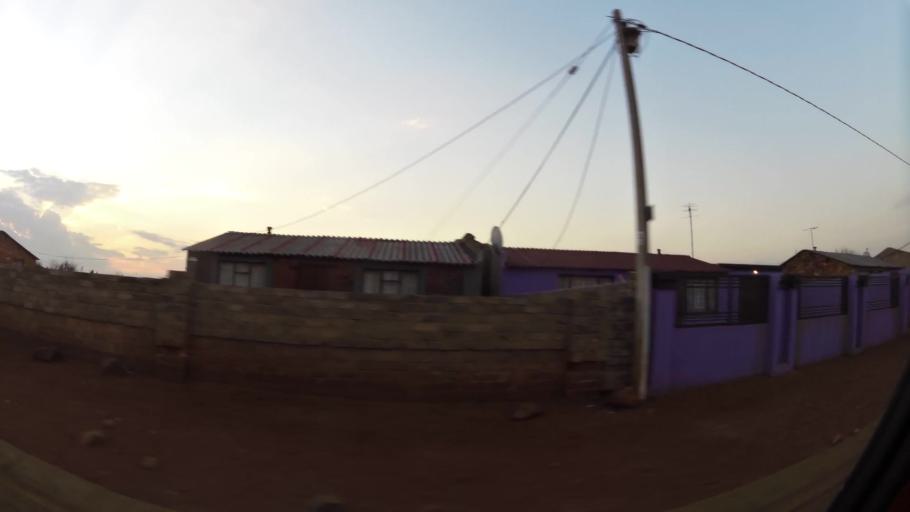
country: ZA
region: Gauteng
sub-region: City of Johannesburg Metropolitan Municipality
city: Orange Farm
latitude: -26.5524
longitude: 27.8756
